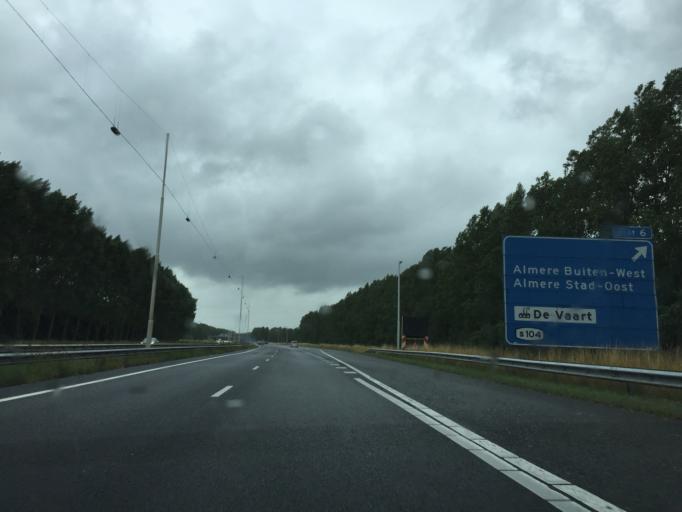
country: NL
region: Flevoland
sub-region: Gemeente Almere
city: Almere Stad
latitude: 52.3674
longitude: 5.2828
